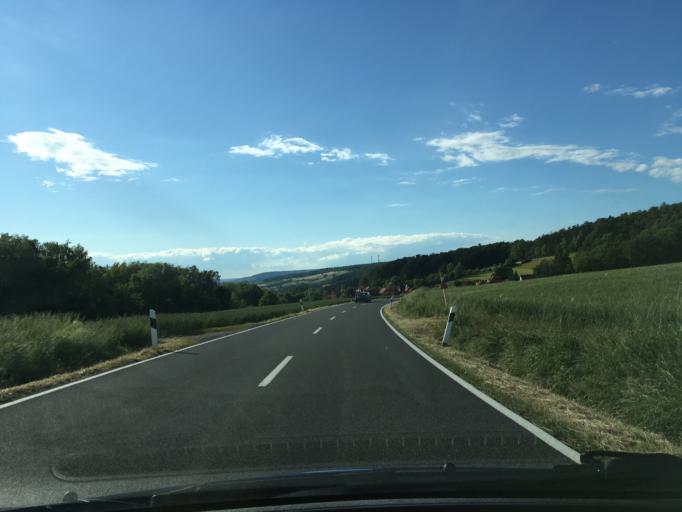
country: DE
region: Lower Saxony
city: Delligsen
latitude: 51.9642
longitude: 9.7713
